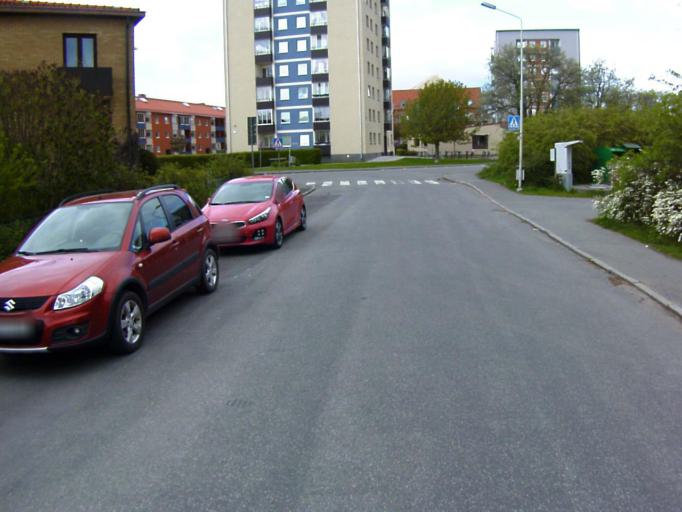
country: SE
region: Skane
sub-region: Kristianstads Kommun
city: Kristianstad
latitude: 56.0355
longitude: 14.1623
